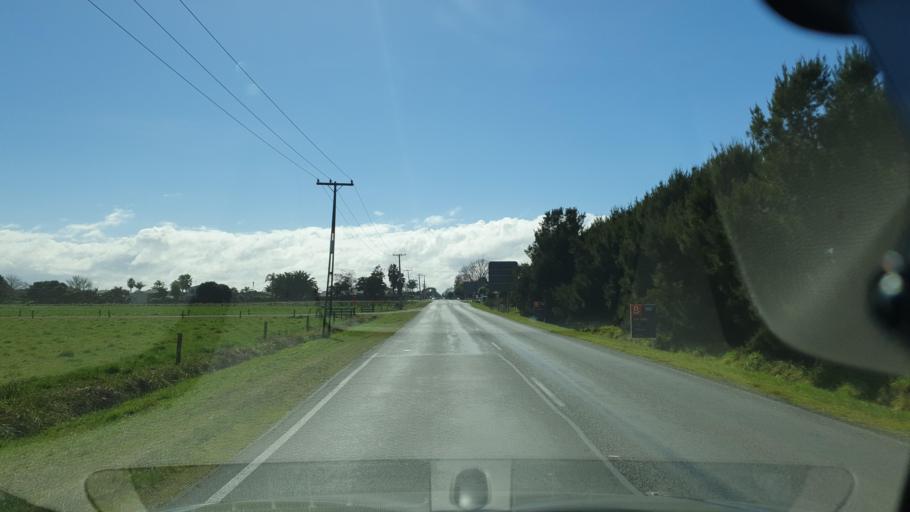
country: NZ
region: Bay of Plenty
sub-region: Tauranga City
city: Tauranga
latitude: -37.7109
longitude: 176.2847
